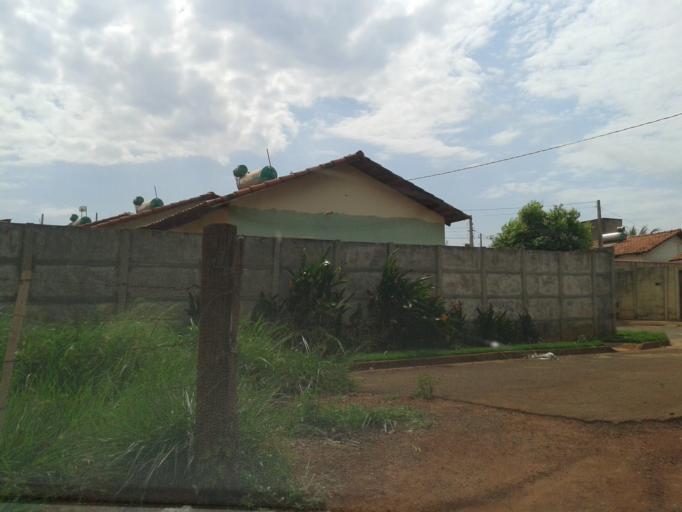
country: BR
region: Minas Gerais
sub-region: Ituiutaba
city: Ituiutaba
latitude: -18.9830
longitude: -49.4412
